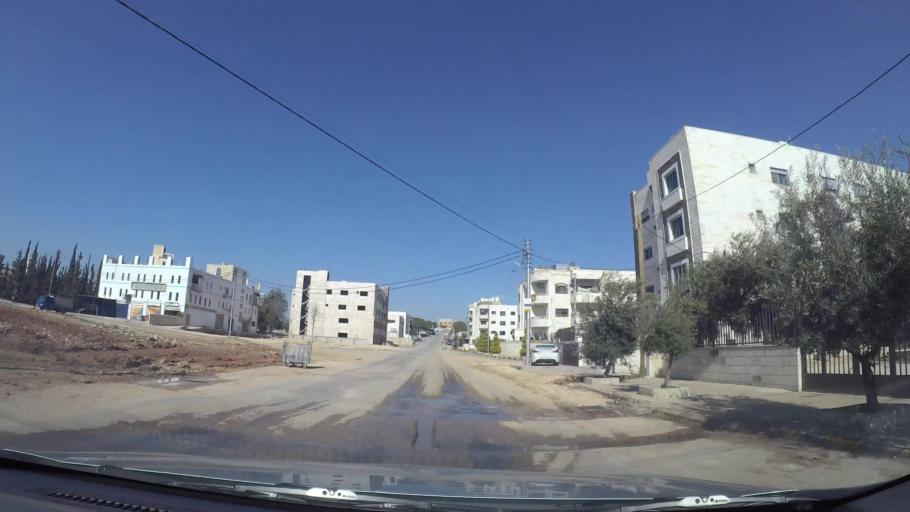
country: JO
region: Amman
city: Al Bunayyat ash Shamaliyah
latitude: 31.9077
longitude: 35.8911
